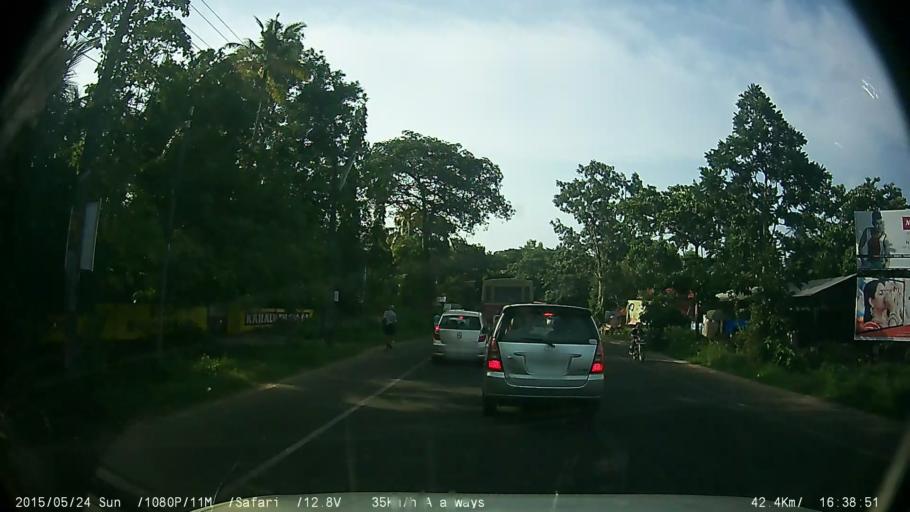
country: IN
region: Kerala
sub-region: Alappuzha
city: Shertallai
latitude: 9.6128
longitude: 76.3302
